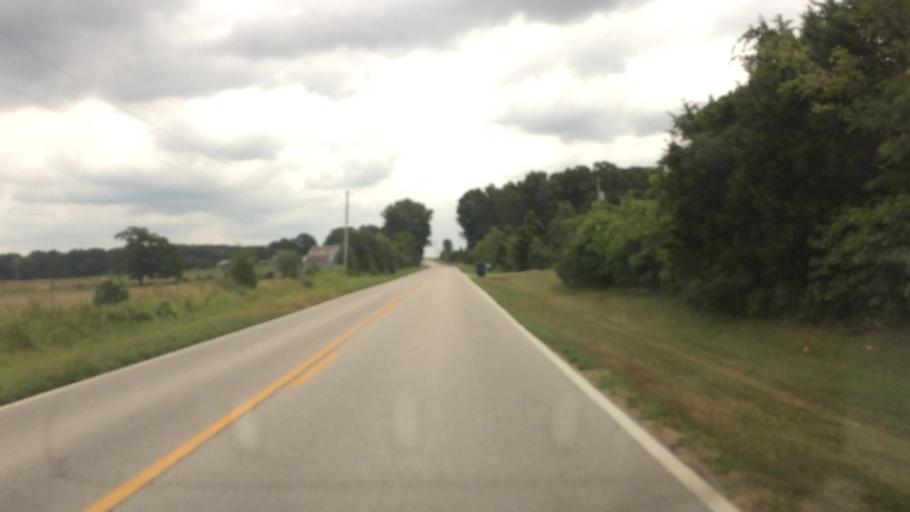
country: US
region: Missouri
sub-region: Greene County
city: Strafford
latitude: 37.2833
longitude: -93.1083
